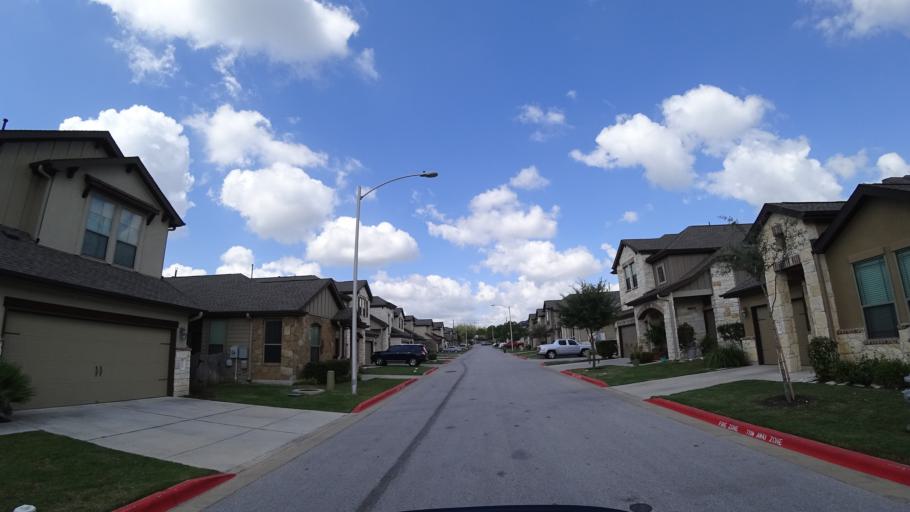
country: US
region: Texas
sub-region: Travis County
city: Manchaca
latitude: 30.1966
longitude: -97.8073
